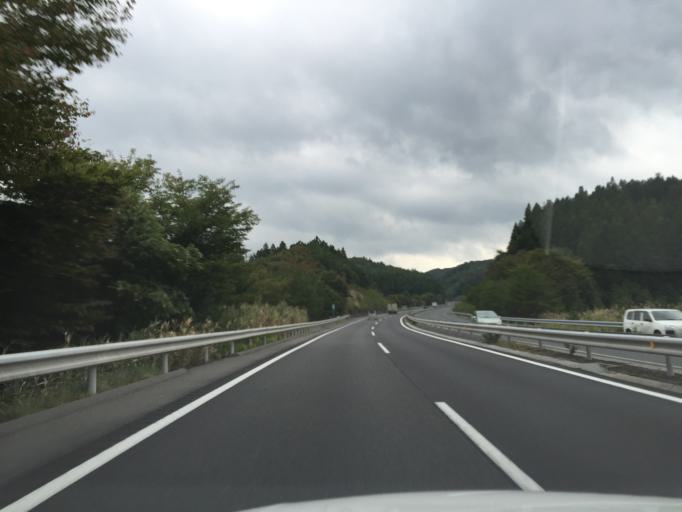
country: JP
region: Fukushima
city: Iwaki
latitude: 37.2080
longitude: 140.6938
